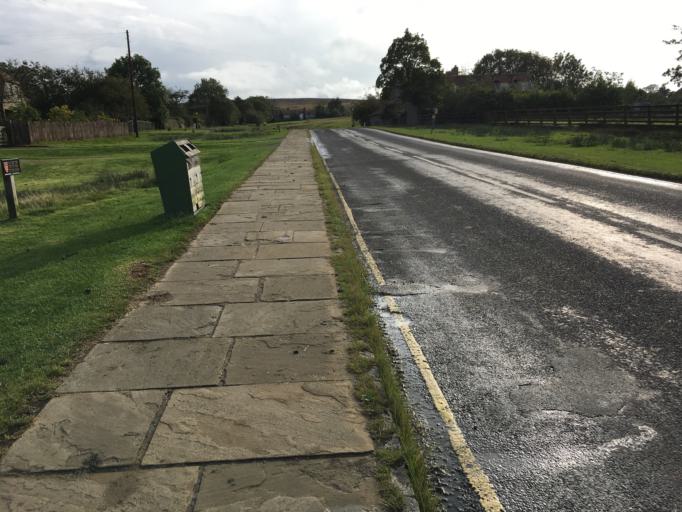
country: GB
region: England
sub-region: North Yorkshire
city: Sleights
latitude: 54.3981
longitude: -0.7223
